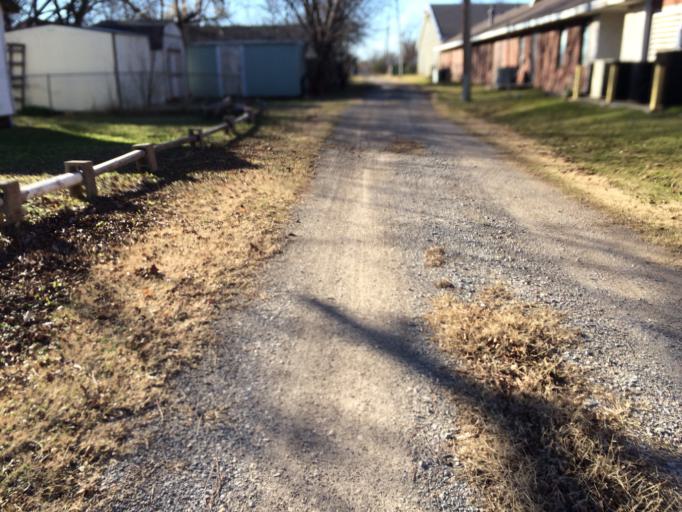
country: US
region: Oklahoma
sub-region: Cleveland County
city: Norman
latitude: 35.2319
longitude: -97.4481
